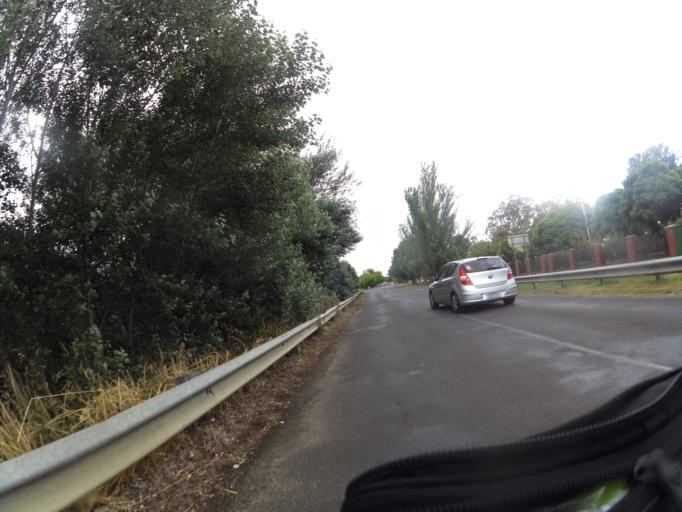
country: AU
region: Victoria
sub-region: Mount Alexander
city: Castlemaine
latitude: -37.0694
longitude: 144.2119
